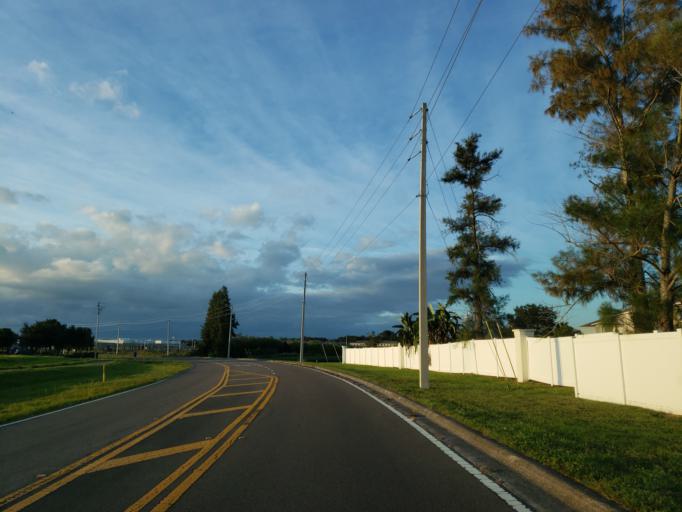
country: US
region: Florida
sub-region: Hillsborough County
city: Riverview
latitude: 27.7956
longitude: -82.3288
